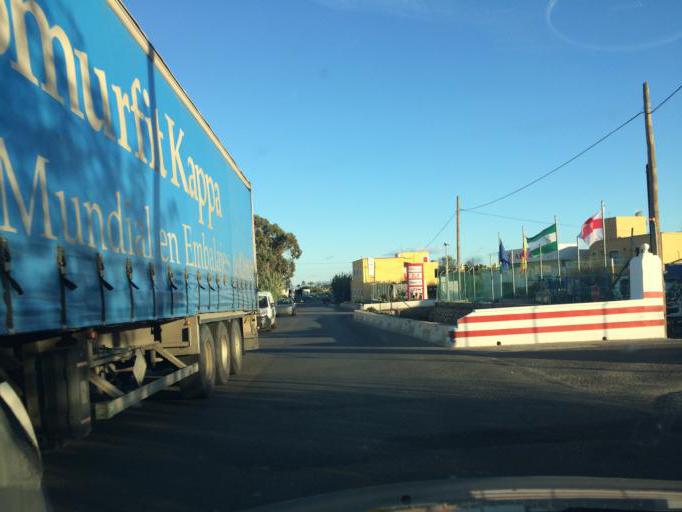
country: ES
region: Andalusia
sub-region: Provincia de Almeria
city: Almeria
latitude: 36.8409
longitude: -2.4244
